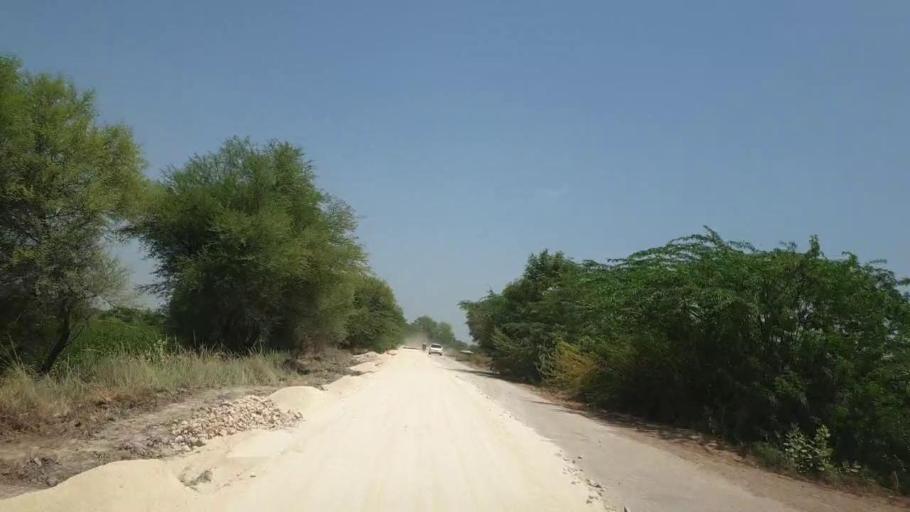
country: PK
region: Sindh
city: Pano Aqil
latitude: 27.6645
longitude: 69.1751
